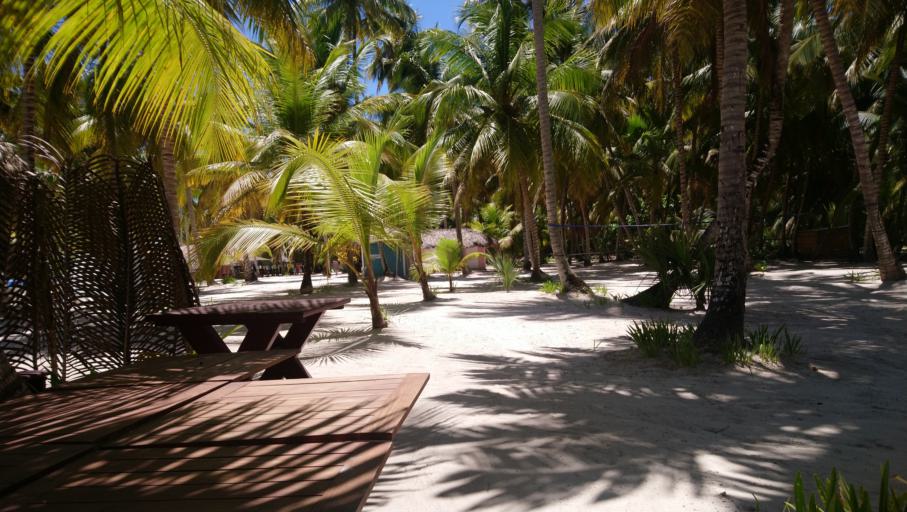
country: DO
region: La Altagracia
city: Boca de Yuma
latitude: 18.1720
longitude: -68.7811
